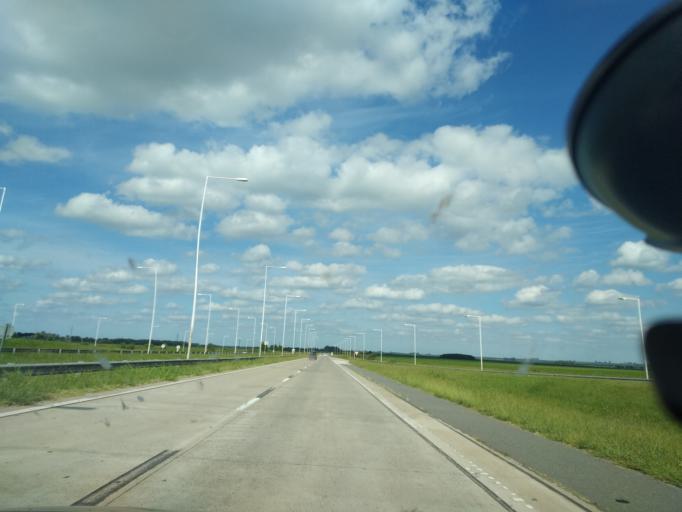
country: AR
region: Santa Fe
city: Carcarana
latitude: -32.8684
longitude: -61.2508
